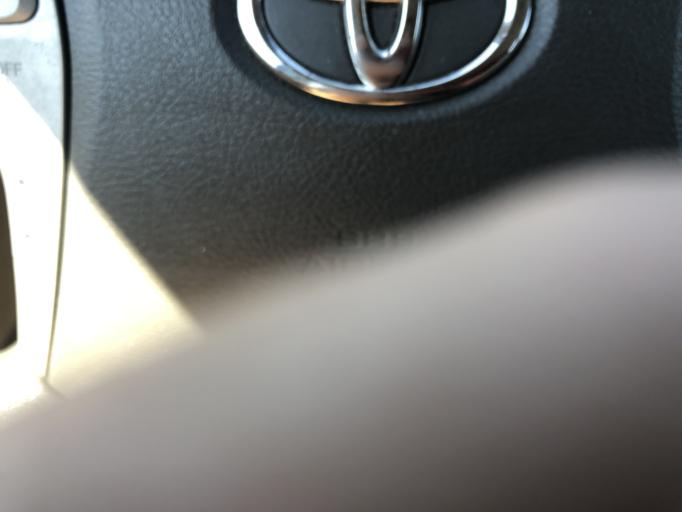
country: US
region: Tennessee
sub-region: Davidson County
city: Forest Hills
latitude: 36.0456
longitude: -86.8565
